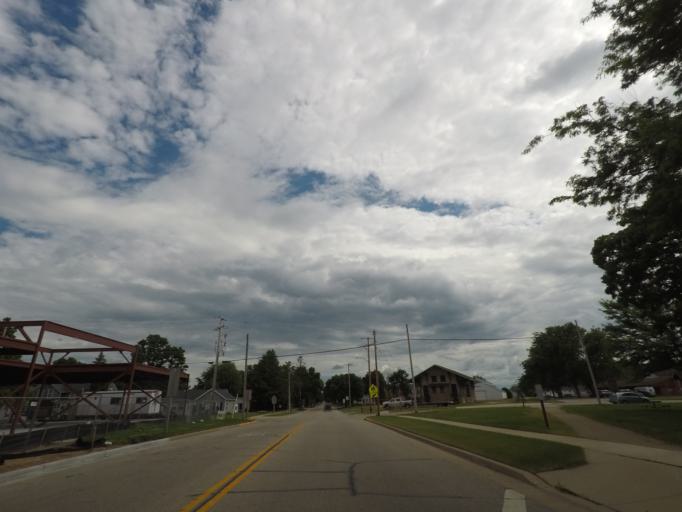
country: US
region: Wisconsin
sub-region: Dane County
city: Belleville
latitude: 42.8592
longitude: -89.5327
